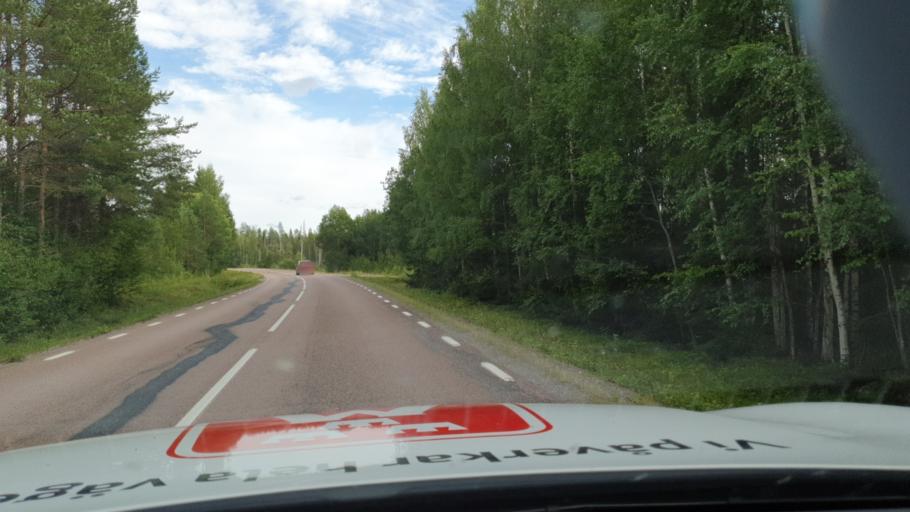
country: SE
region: Jaemtland
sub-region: Stroemsunds Kommun
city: Stroemsund
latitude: 63.6345
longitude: 16.0432
